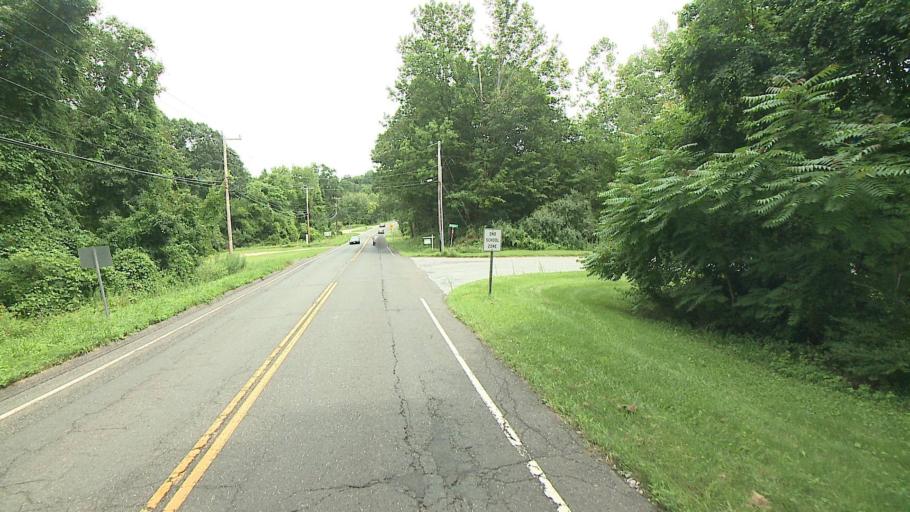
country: US
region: Connecticut
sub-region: Fairfield County
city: Newtown
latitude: 41.4675
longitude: -73.3845
